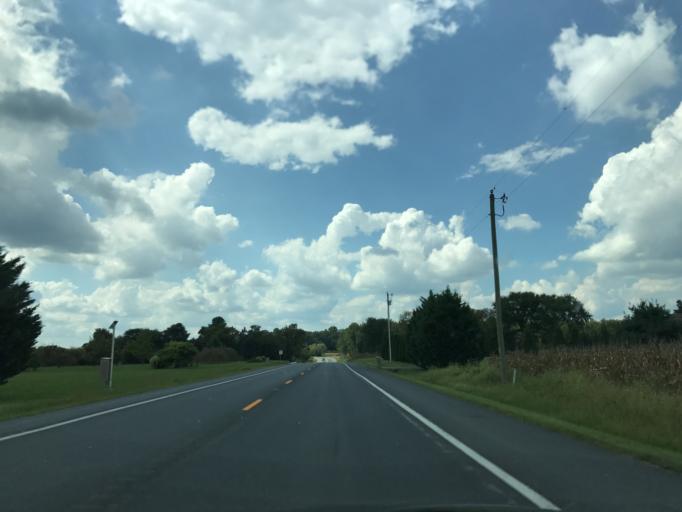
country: US
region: Delaware
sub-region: Kent County
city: Clayton
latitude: 39.1998
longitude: -75.7498
